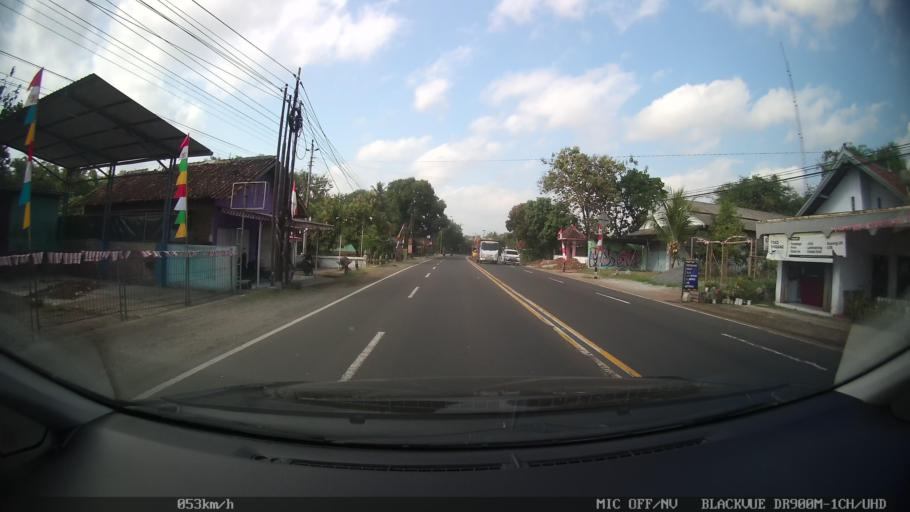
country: ID
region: Daerah Istimewa Yogyakarta
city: Godean
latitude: -7.8381
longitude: 110.2199
